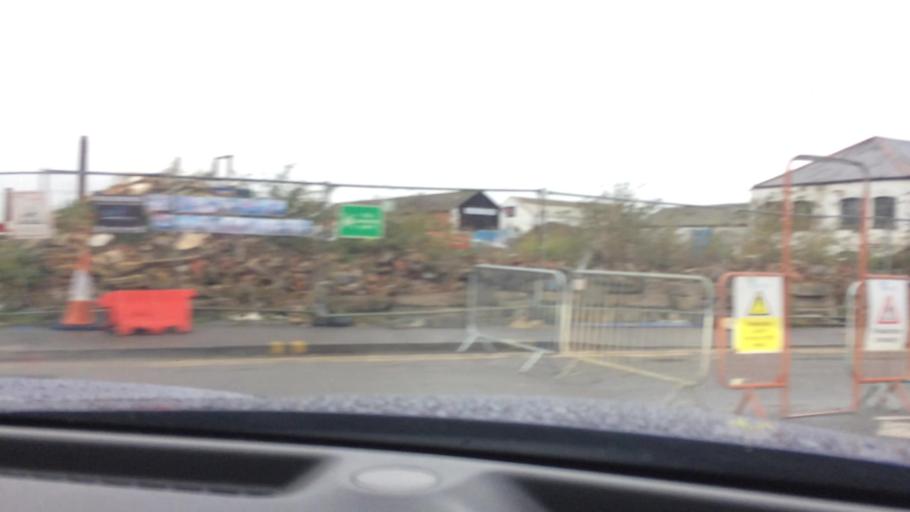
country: GB
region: England
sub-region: Poole
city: Poole
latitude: 50.7132
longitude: -1.9918
